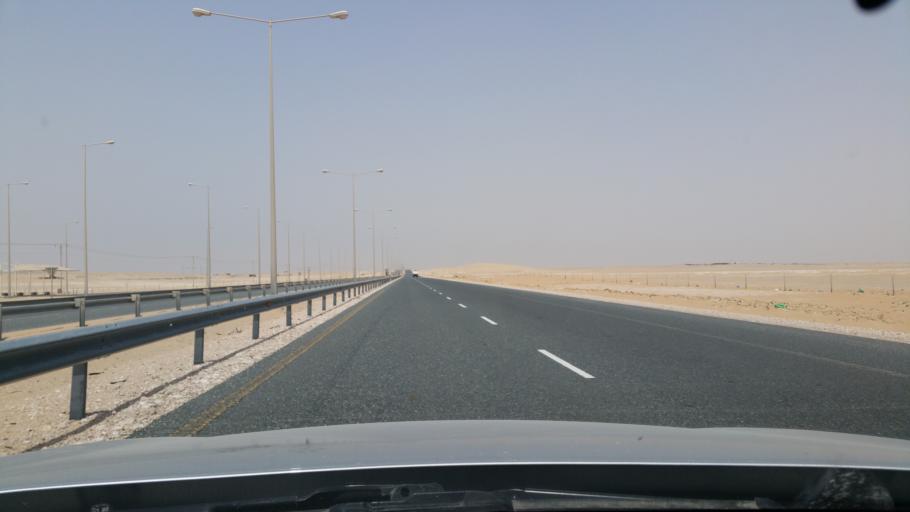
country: QA
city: Umm Bab
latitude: 24.9699
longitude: 50.9549
